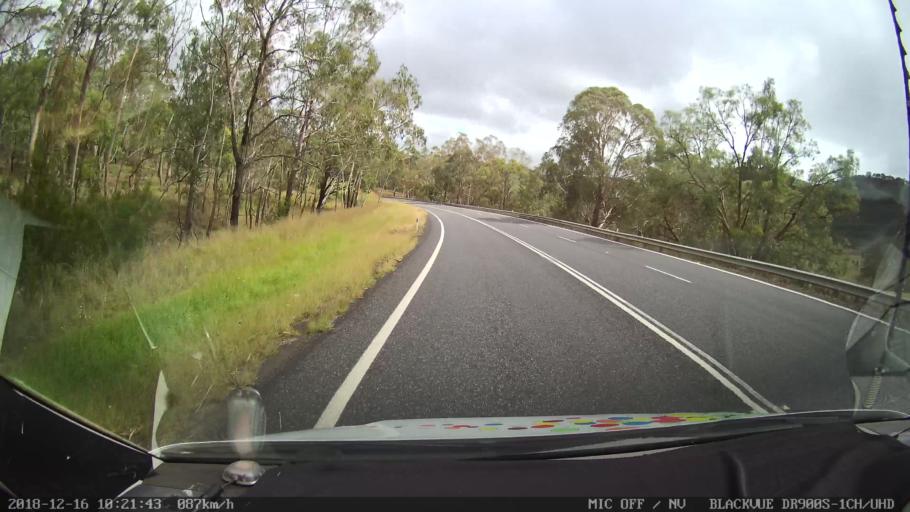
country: AU
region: New South Wales
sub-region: Tenterfield Municipality
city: Carrolls Creek
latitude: -29.2033
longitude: 152.0139
